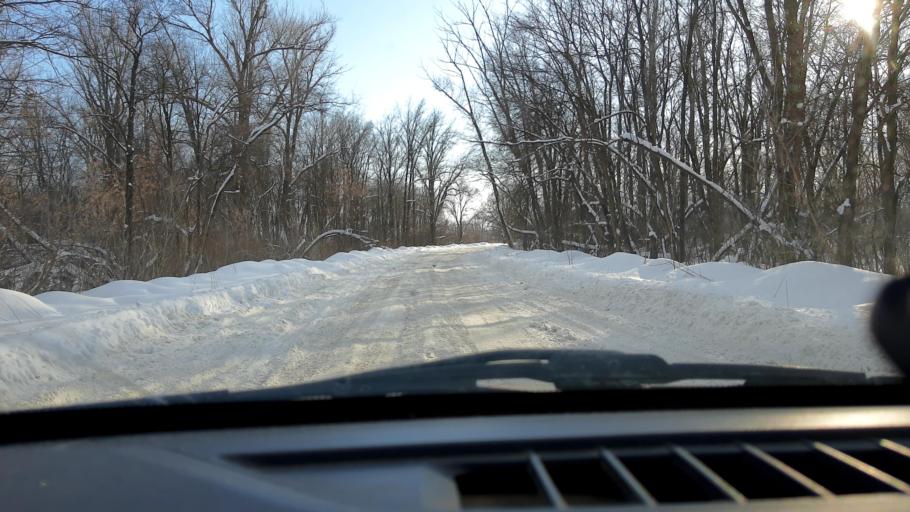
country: RU
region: Bashkortostan
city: Ufa
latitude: 54.6369
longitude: 56.0055
